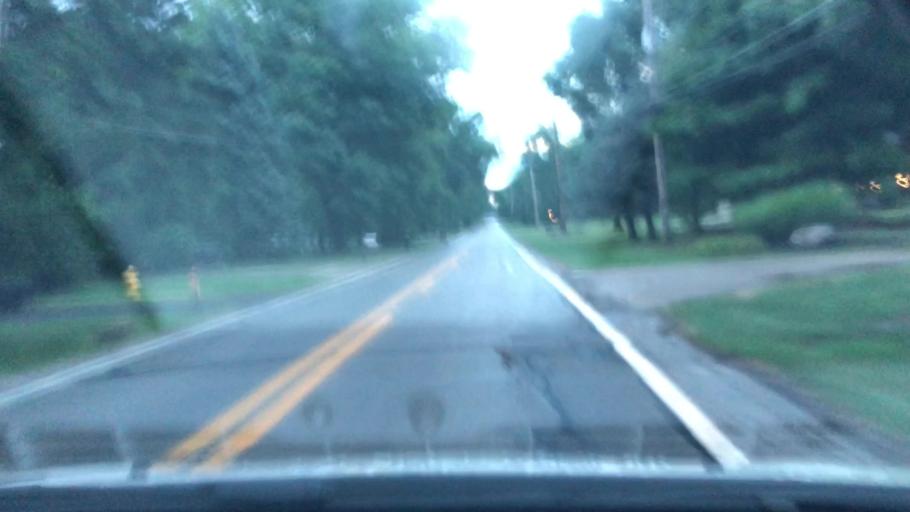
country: US
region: Ohio
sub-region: Franklin County
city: Huber Ridge
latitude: 40.1048
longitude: -82.8639
